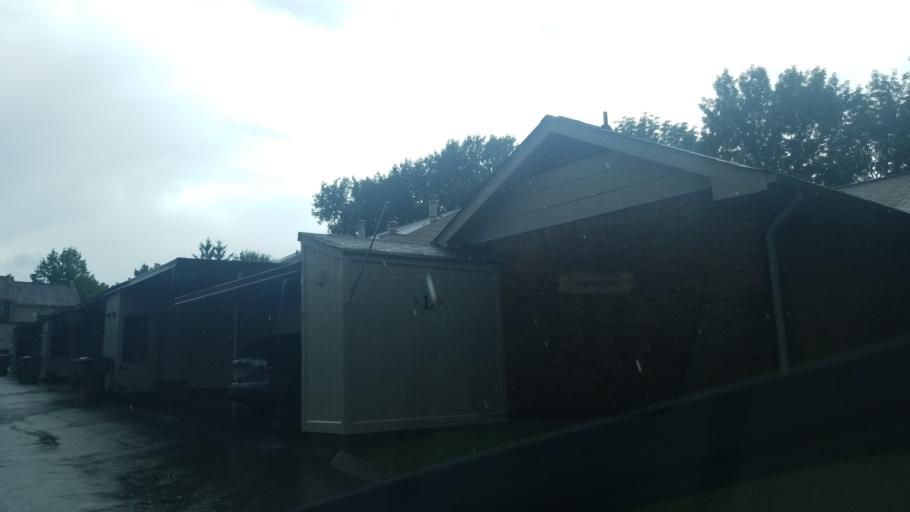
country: US
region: Tennessee
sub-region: Rutherford County
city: La Vergne
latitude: 36.1047
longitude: -86.6022
